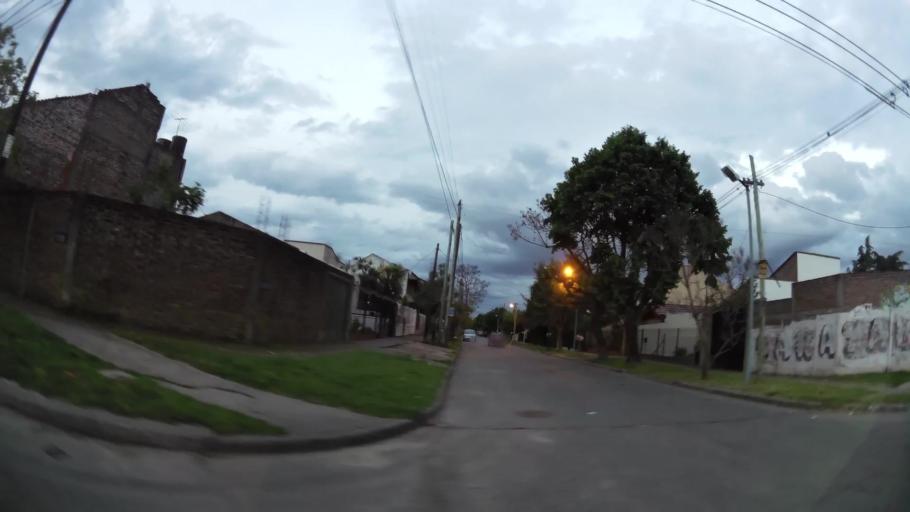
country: AR
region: Buenos Aires
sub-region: Partido de Quilmes
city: Quilmes
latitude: -34.7393
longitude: -58.2303
